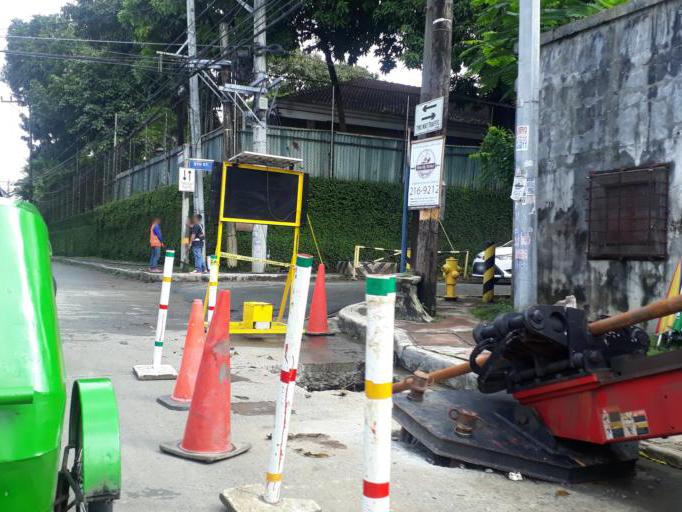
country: PH
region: Metro Manila
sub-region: San Juan
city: San Juan
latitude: 14.6166
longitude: 121.0272
